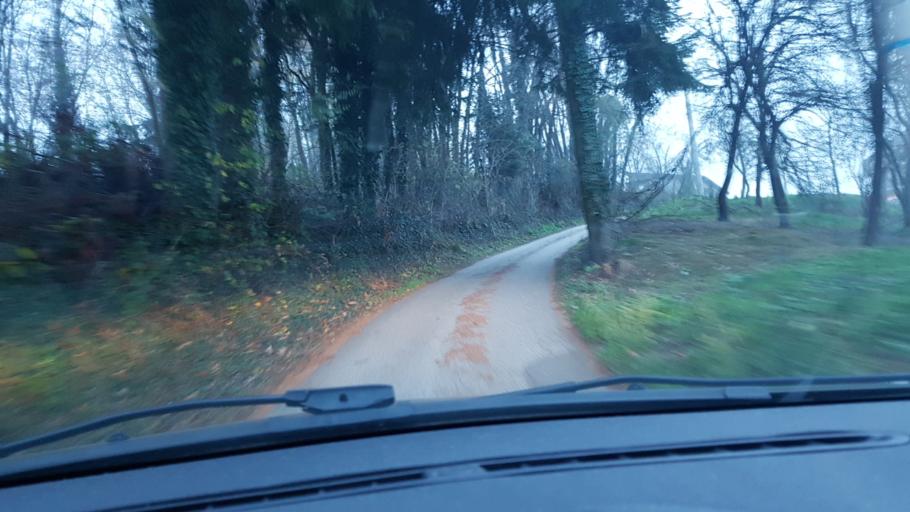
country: HR
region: Krapinsko-Zagorska
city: Pregrada
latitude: 46.2037
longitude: 15.7885
